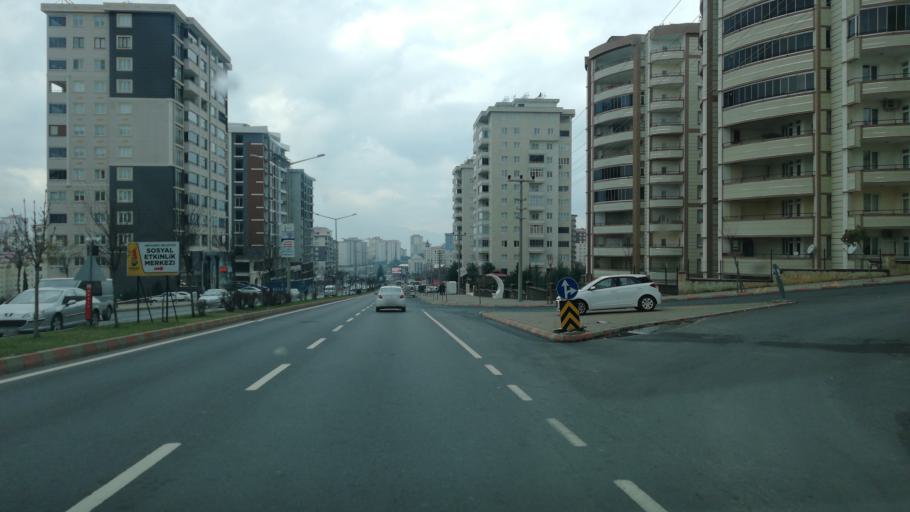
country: TR
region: Kahramanmaras
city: Kahramanmaras
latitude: 37.5831
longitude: 36.8748
